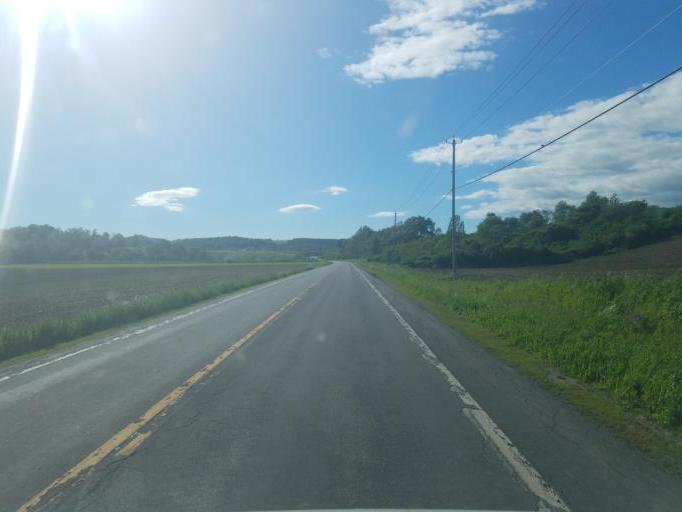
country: US
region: New York
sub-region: Herkimer County
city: Little Falls
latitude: 43.0131
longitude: -74.8021
